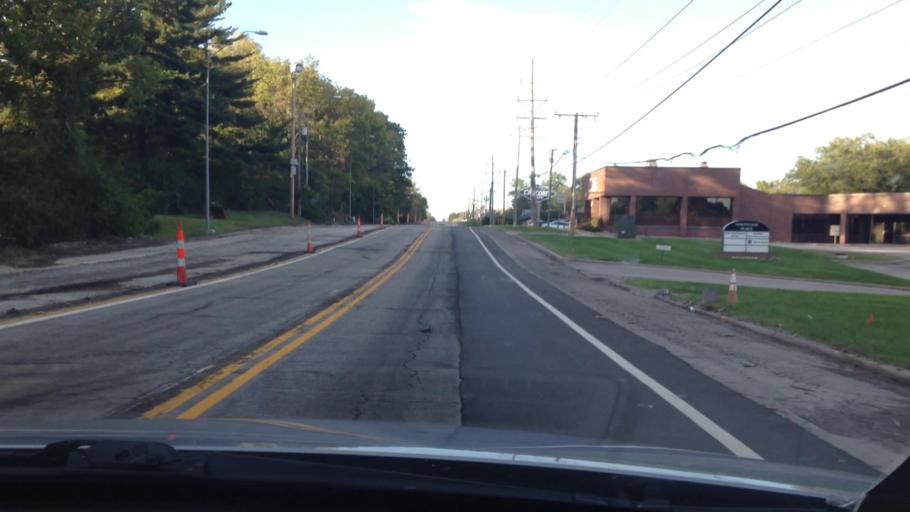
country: US
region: Missouri
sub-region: Clay County
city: North Kansas City
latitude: 39.1611
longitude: -94.5769
